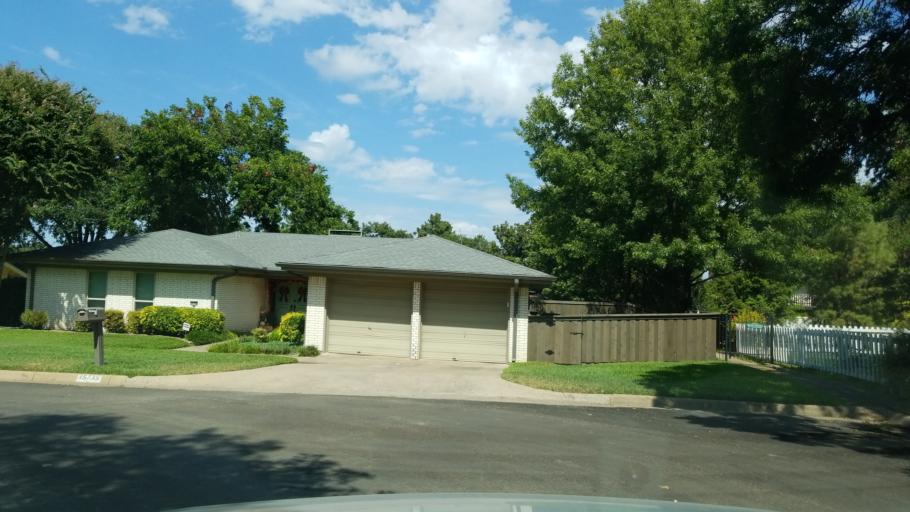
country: US
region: Texas
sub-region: Dallas County
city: Addison
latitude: 32.9629
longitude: -96.7836
